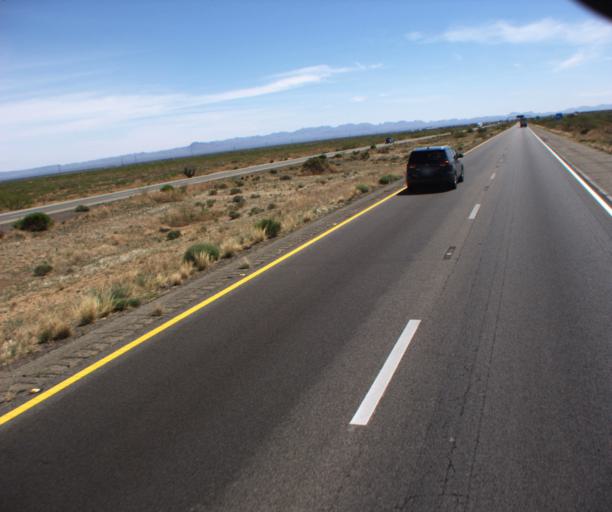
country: US
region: Arizona
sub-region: Cochise County
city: Willcox
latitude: 32.3351
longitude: -109.5347
